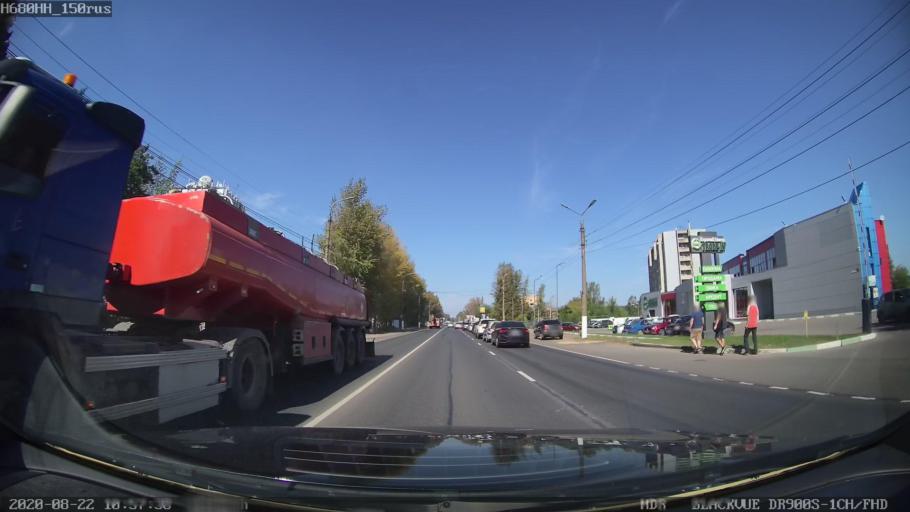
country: RU
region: Tverskaya
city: Tver
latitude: 56.8141
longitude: 35.9920
